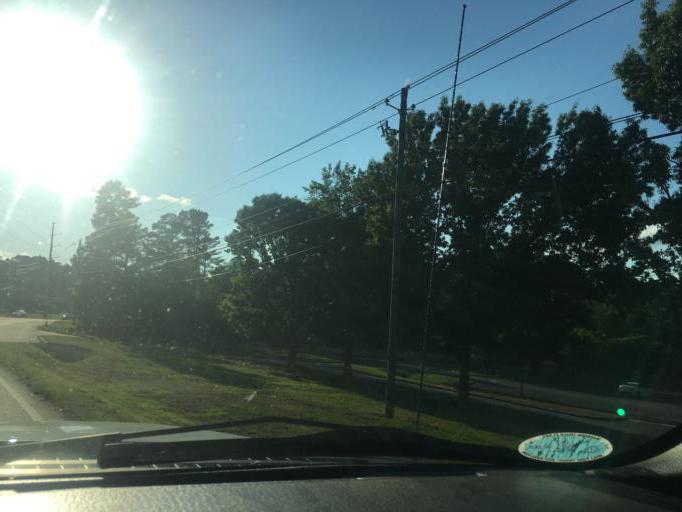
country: US
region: Georgia
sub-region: Forsyth County
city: Cumming
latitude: 34.2729
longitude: -84.1064
